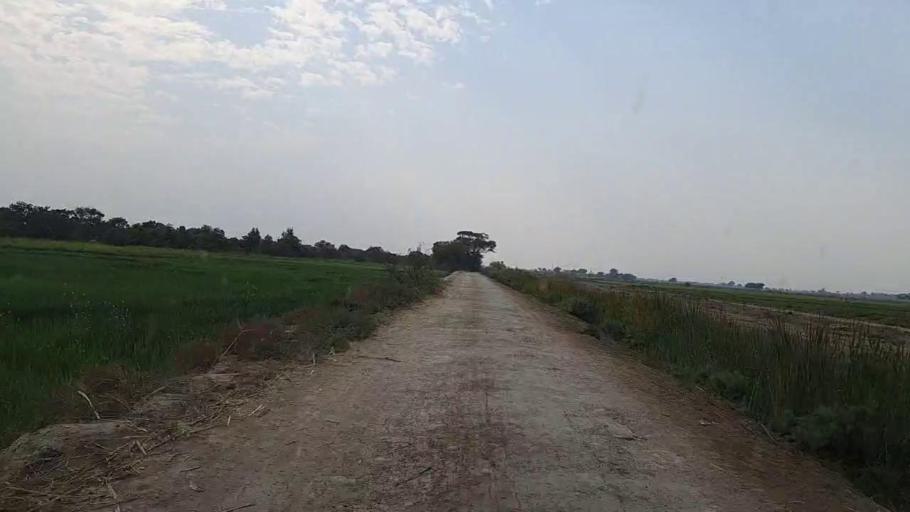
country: PK
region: Sindh
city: Mirwah Gorchani
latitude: 25.3717
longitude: 69.0776
